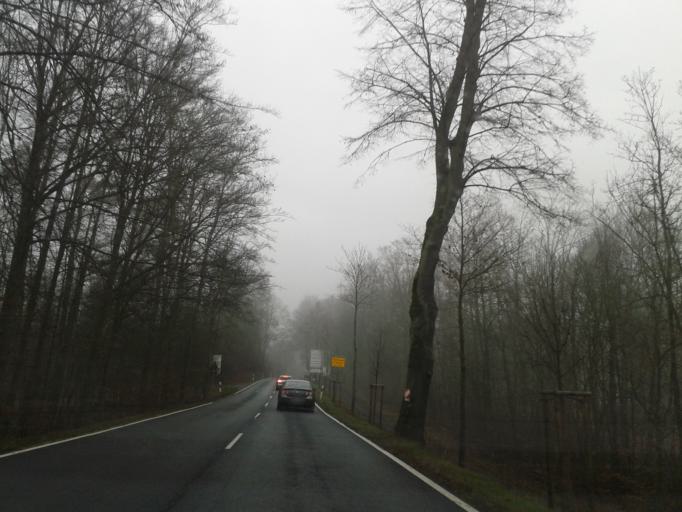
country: DE
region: Bavaria
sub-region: Upper Franconia
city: Weitramsdorf
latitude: 50.2315
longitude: 10.8606
